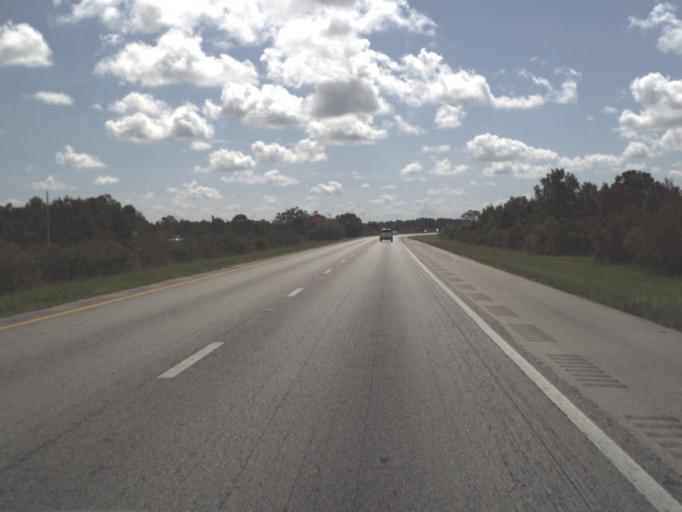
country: US
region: Florida
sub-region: Lee County
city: Suncoast Estates
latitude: 26.7730
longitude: -81.8839
